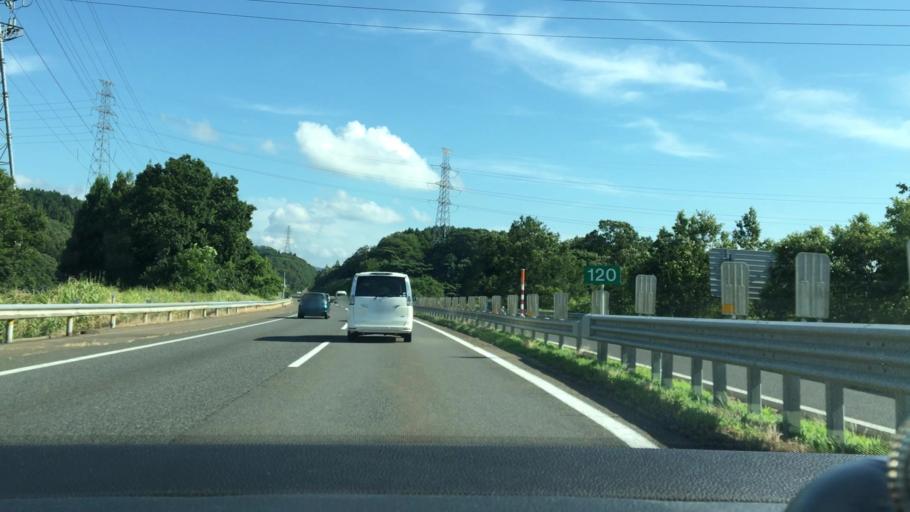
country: JP
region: Fukui
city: Maruoka
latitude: 36.2269
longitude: 136.2802
